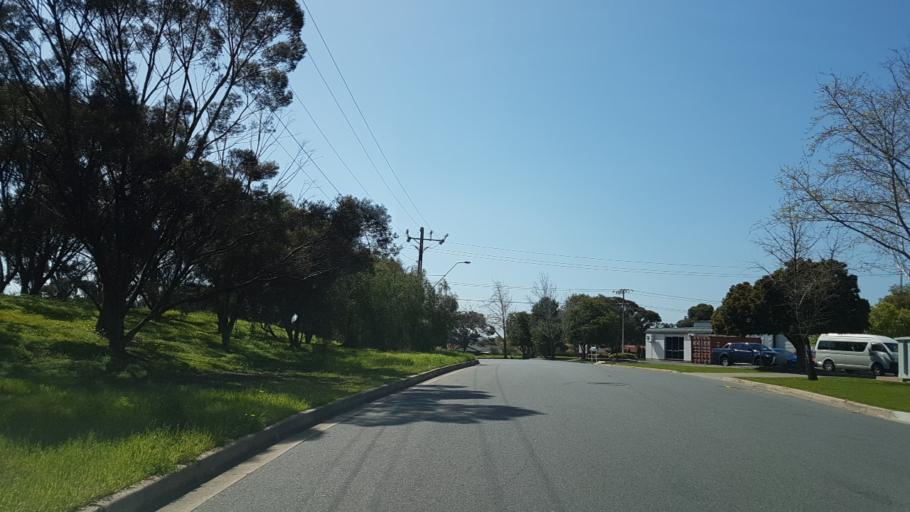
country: AU
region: South Australia
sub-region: Tea Tree Gully
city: Modbury
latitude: -34.8454
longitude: 138.6785
